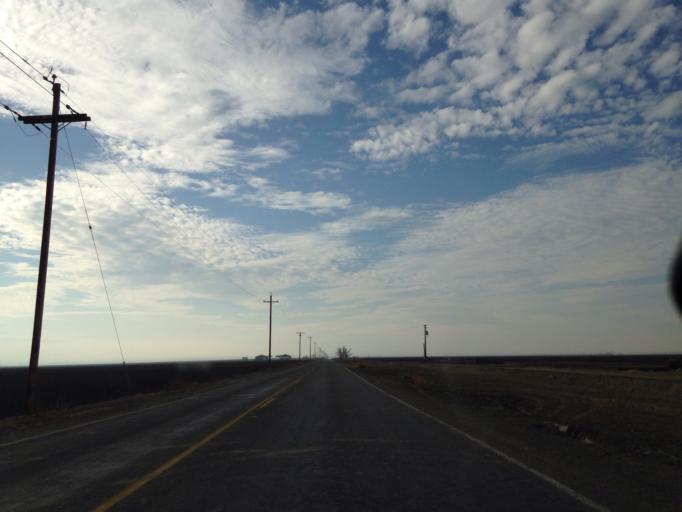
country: US
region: California
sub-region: Kern County
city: Buttonwillow
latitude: 35.4421
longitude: -119.5190
